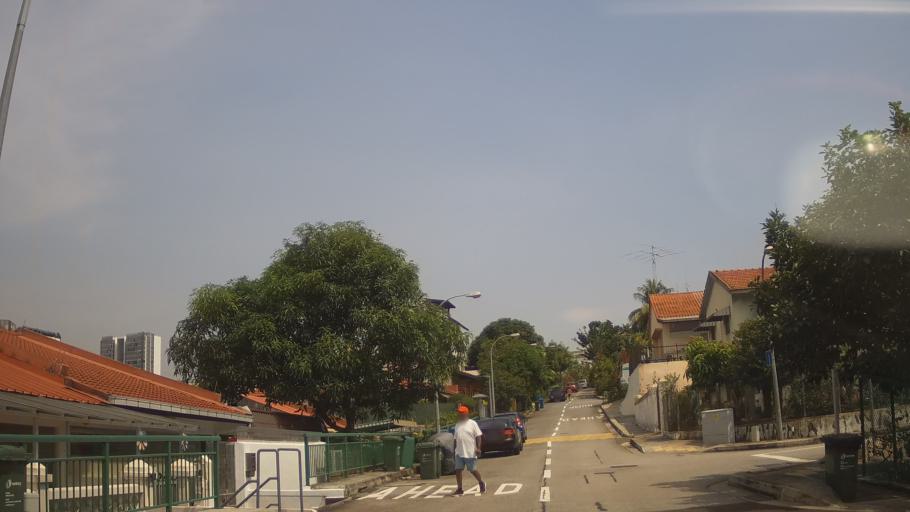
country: MY
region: Johor
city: Johor Bahru
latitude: 1.3591
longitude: 103.7681
